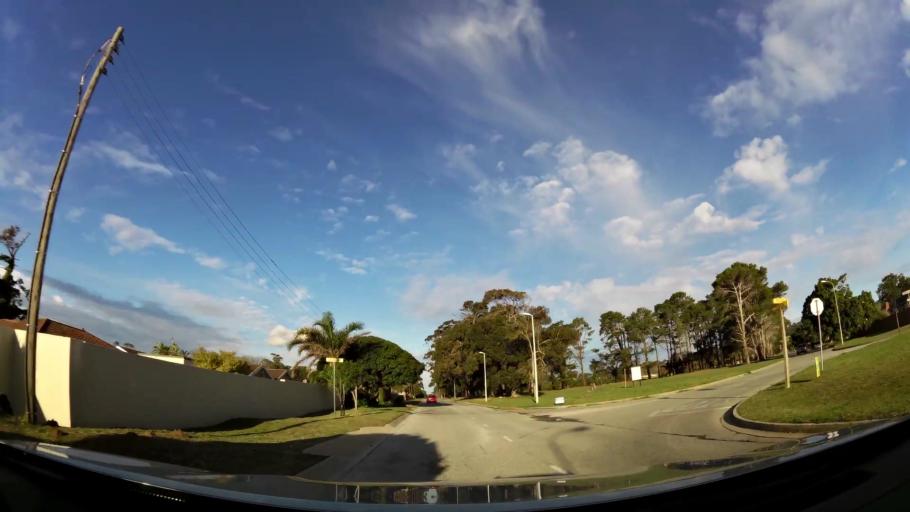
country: ZA
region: Eastern Cape
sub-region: Nelson Mandela Bay Metropolitan Municipality
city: Port Elizabeth
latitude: -33.9749
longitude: 25.5047
